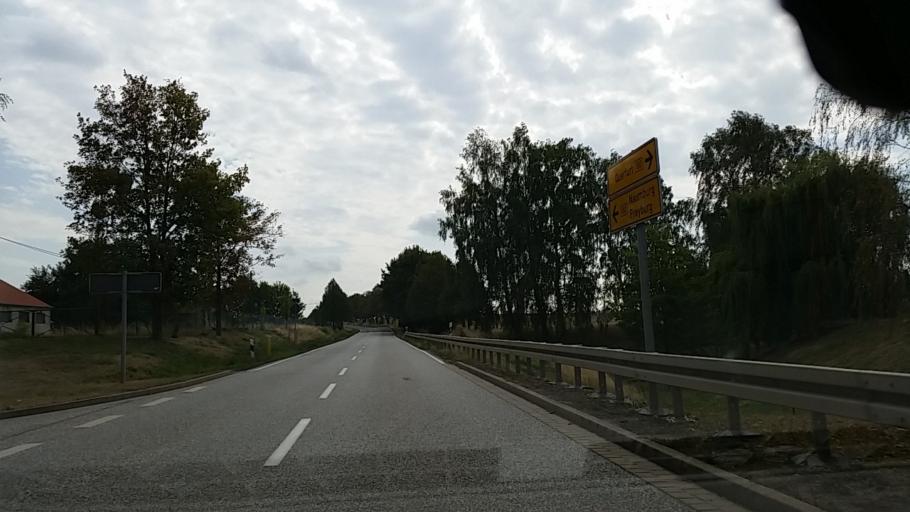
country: DE
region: Saxony-Anhalt
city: Nemsdorf-Gohrendorf
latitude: 51.3402
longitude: 11.6401
